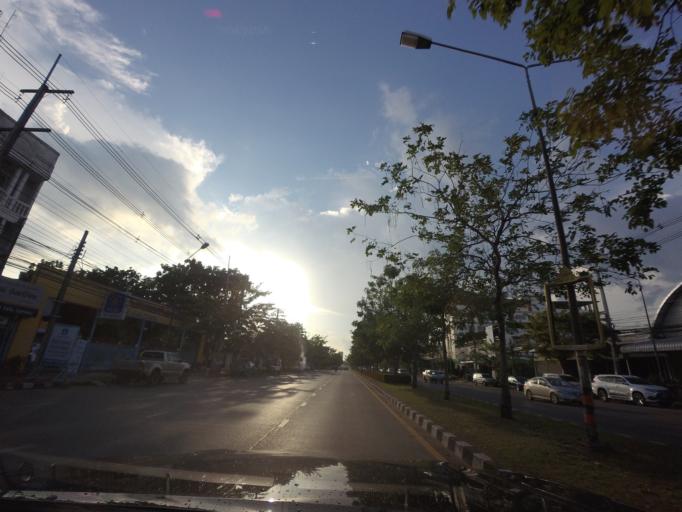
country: TH
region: Khon Kaen
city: Khon Kaen
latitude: 16.4282
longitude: 102.8589
